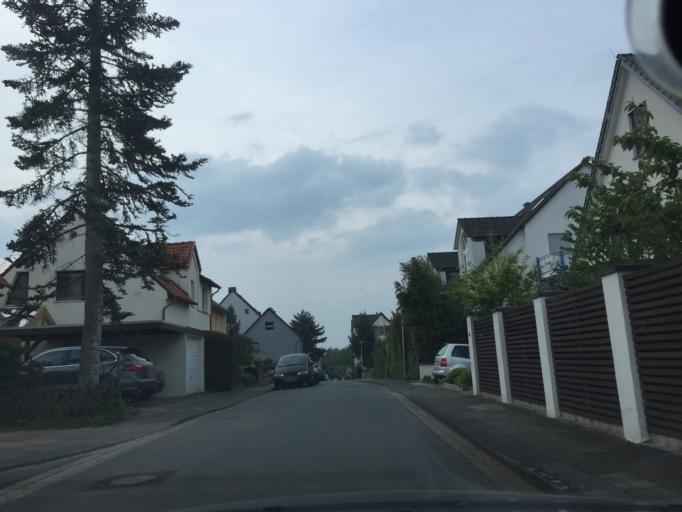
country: DE
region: Lower Saxony
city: Hildesheim
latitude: 52.1503
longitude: 9.9249
